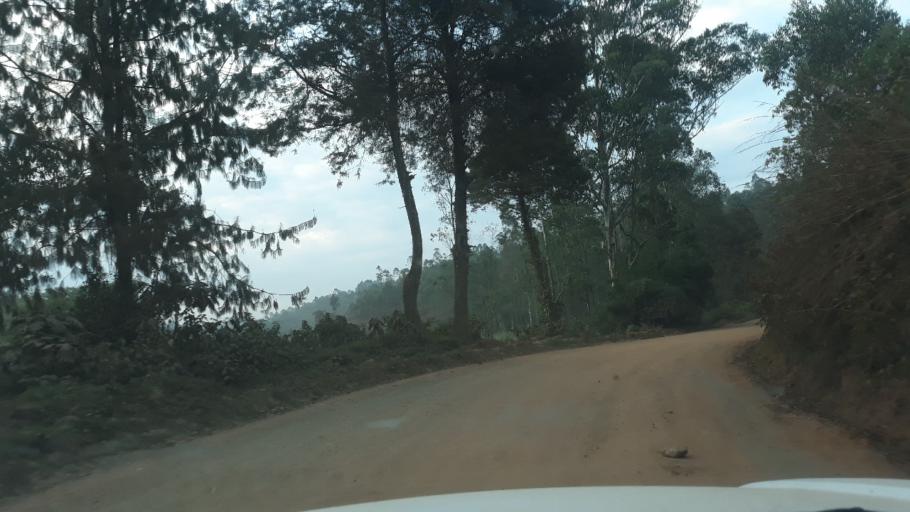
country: CD
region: South Kivu
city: Bukavu
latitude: -2.6374
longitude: 28.8755
